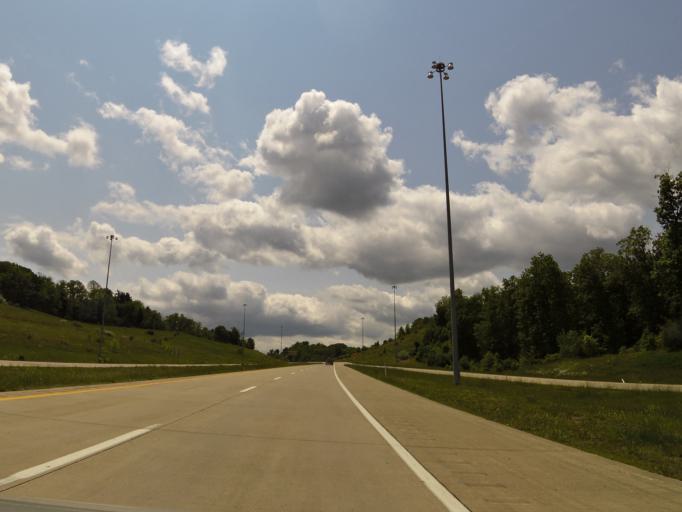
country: US
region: Ohio
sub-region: Athens County
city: Athens
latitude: 39.2991
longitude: -82.1028
